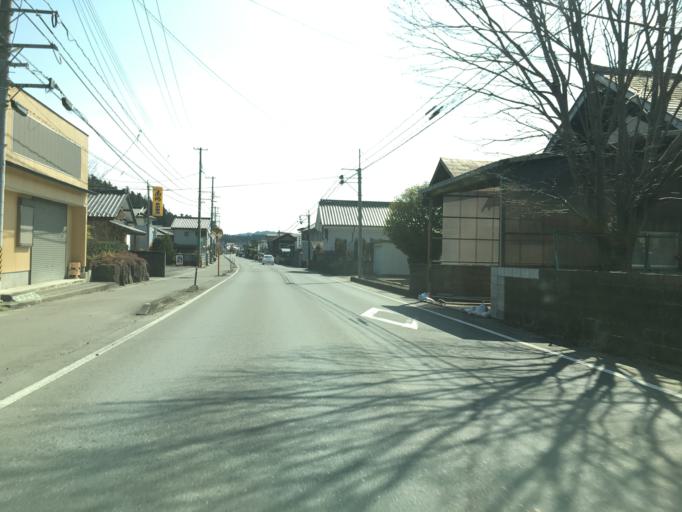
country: JP
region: Ibaraki
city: Daigo
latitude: 36.8942
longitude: 140.4194
